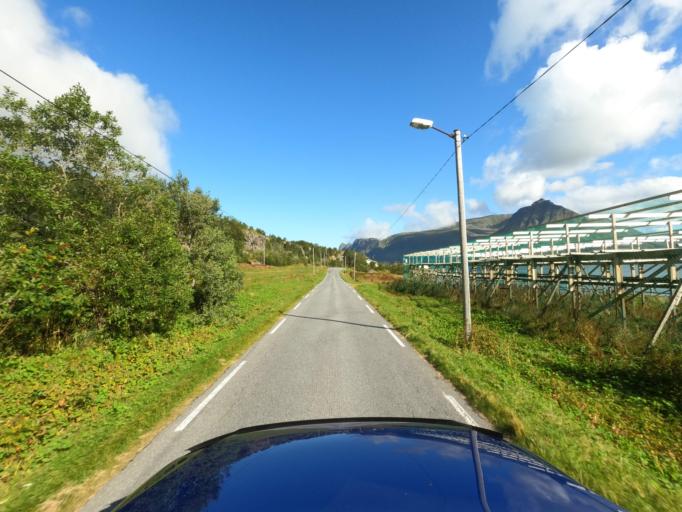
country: NO
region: Nordland
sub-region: Vagan
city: Kabelvag
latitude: 68.2803
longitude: 14.2616
